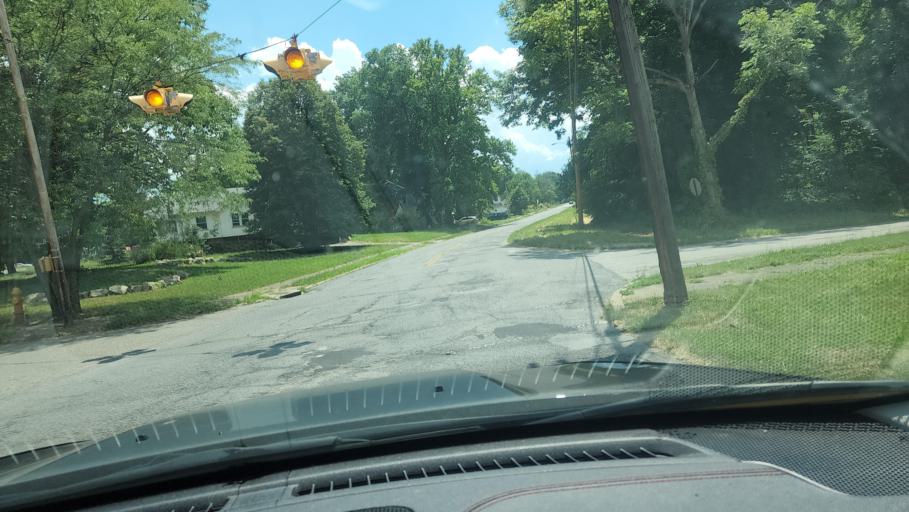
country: US
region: Ohio
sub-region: Mahoning County
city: Struthers
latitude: 41.0646
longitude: -80.6198
